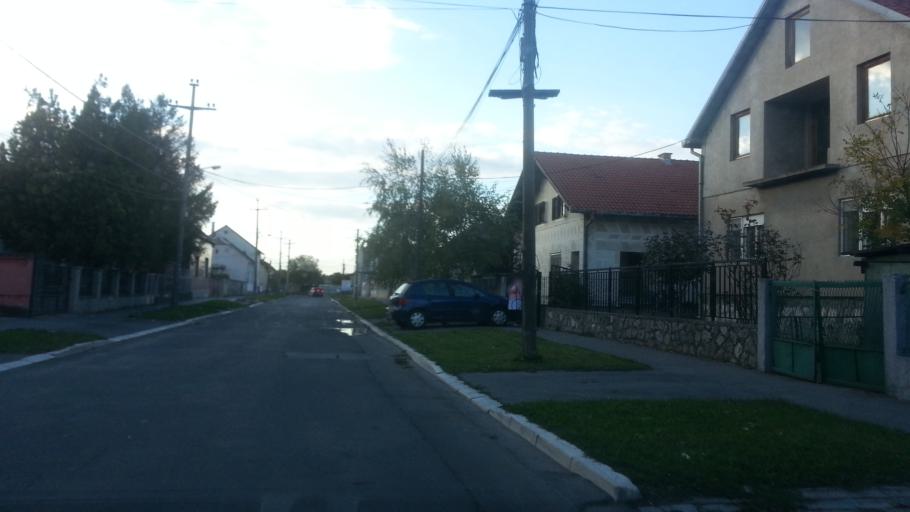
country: RS
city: Novi Banovci
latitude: 44.9010
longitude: 20.2760
